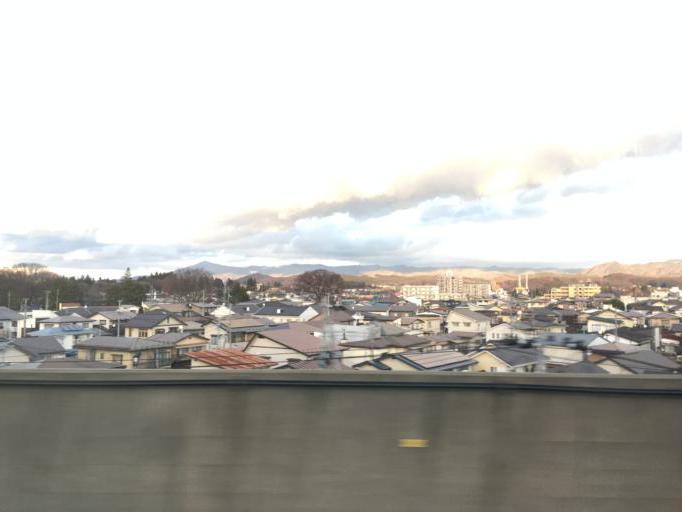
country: JP
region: Iwate
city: Morioka-shi
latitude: 39.7148
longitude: 141.1218
